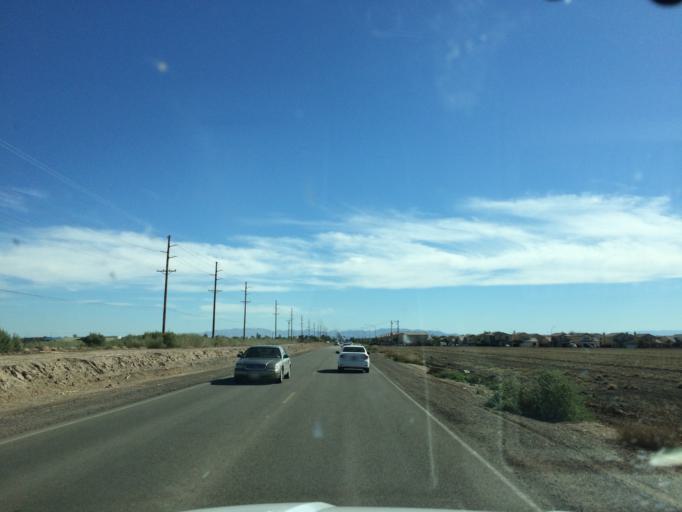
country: US
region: California
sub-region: Imperial County
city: Heber
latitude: 32.7442
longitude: -115.5347
